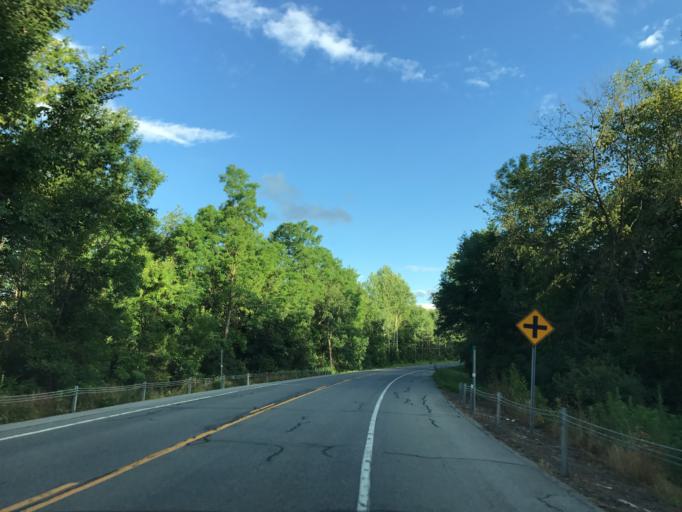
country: US
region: New York
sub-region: Saratoga County
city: Schuylerville
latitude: 43.1560
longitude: -73.5752
